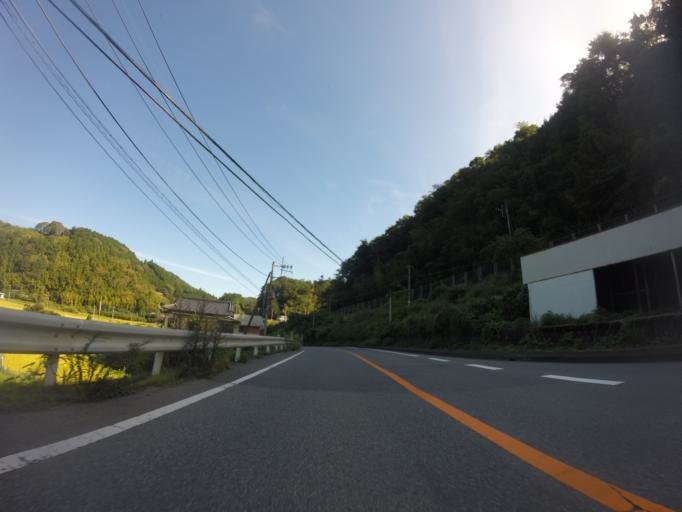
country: JP
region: Shizuoka
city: Fujinomiya
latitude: 35.3406
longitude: 138.4498
